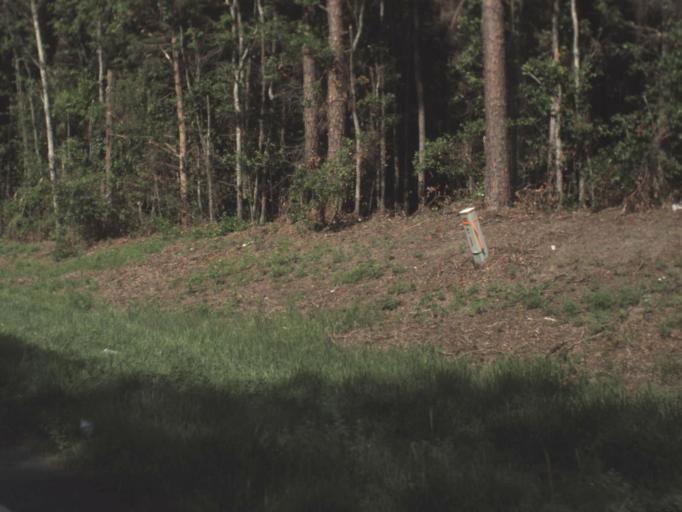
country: US
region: Florida
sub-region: Madison County
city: Madison
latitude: 30.4793
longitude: -83.3953
